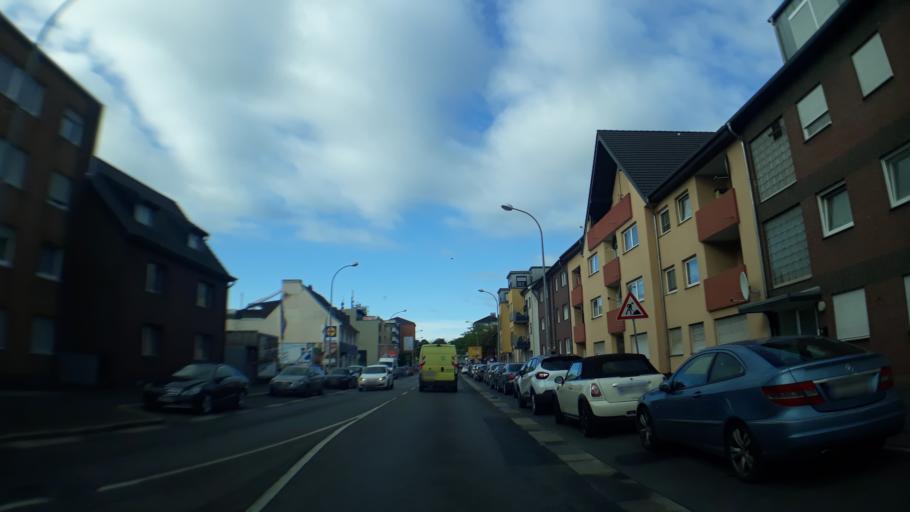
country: DE
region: North Rhine-Westphalia
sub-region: Regierungsbezirk Koln
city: Hurth
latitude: 50.8789
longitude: 6.8890
